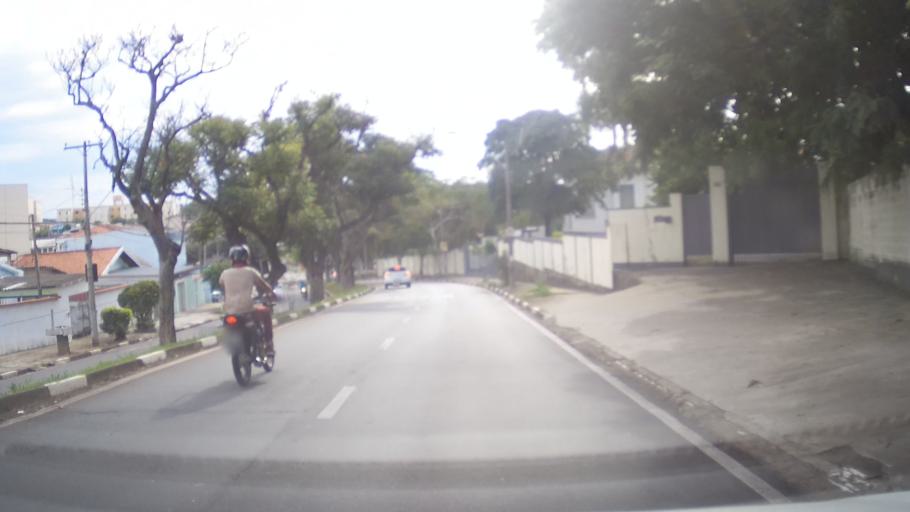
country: BR
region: Sao Paulo
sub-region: Campinas
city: Campinas
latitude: -22.8996
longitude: -47.1004
